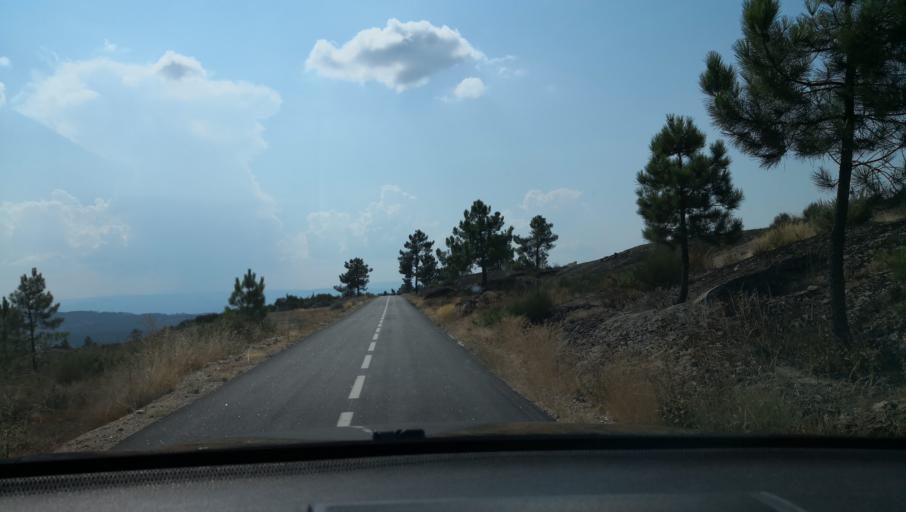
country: PT
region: Vila Real
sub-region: Sabrosa
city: Sabrosa
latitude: 41.2818
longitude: -7.6148
